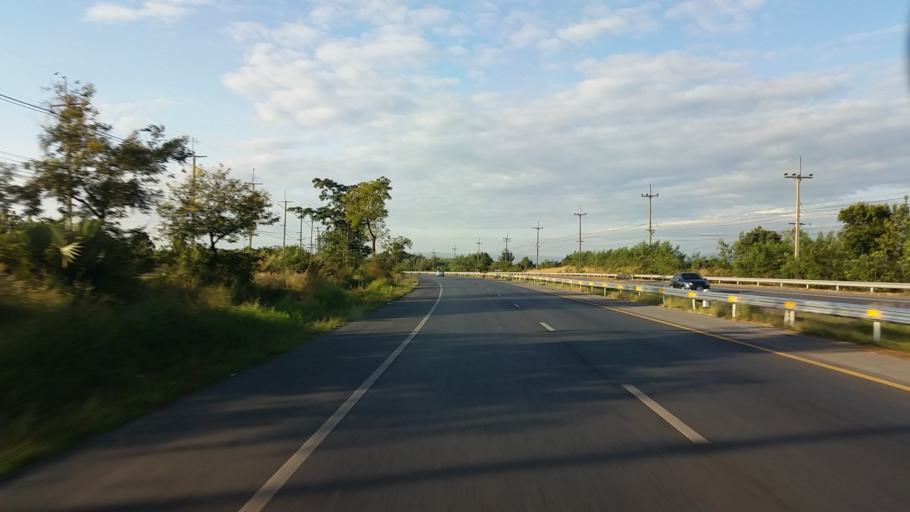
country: TH
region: Lop Buri
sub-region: Amphoe Tha Luang
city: Tha Luang
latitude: 15.0494
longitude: 100.9611
